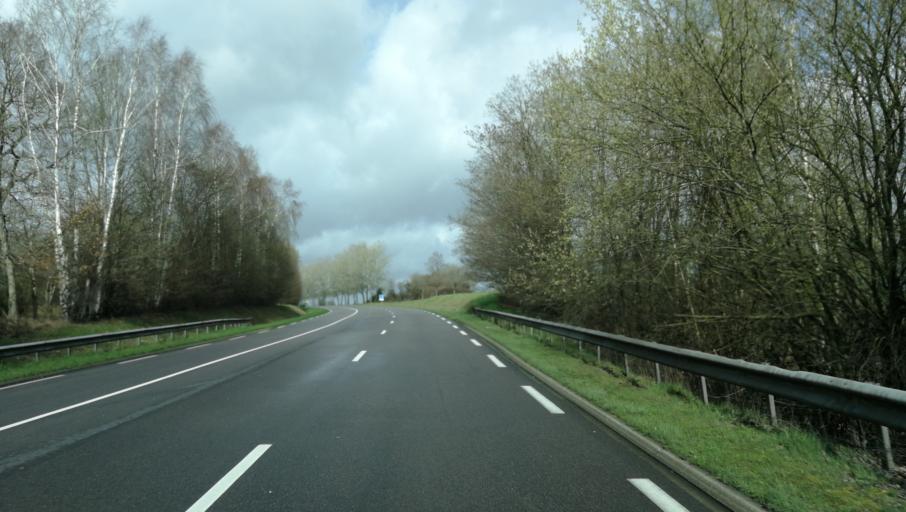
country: FR
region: Haute-Normandie
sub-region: Departement de l'Eure
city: Lieurey
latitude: 49.2514
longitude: 0.4676
